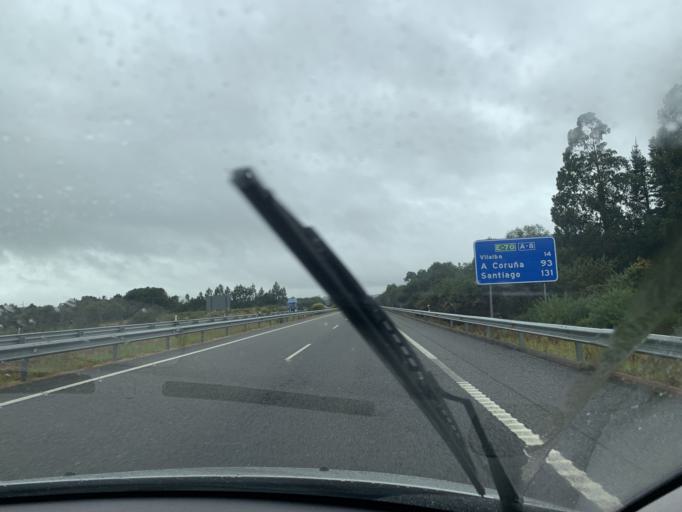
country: ES
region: Galicia
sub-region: Provincia de Lugo
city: Abadin
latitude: 43.3379
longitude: -7.5565
